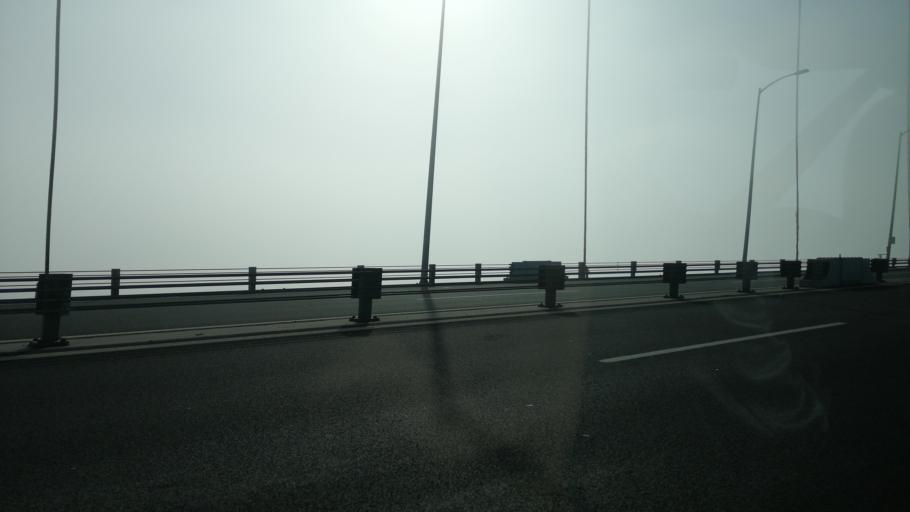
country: TR
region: Kocaeli
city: Tavsancil
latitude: 40.7591
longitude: 29.5165
